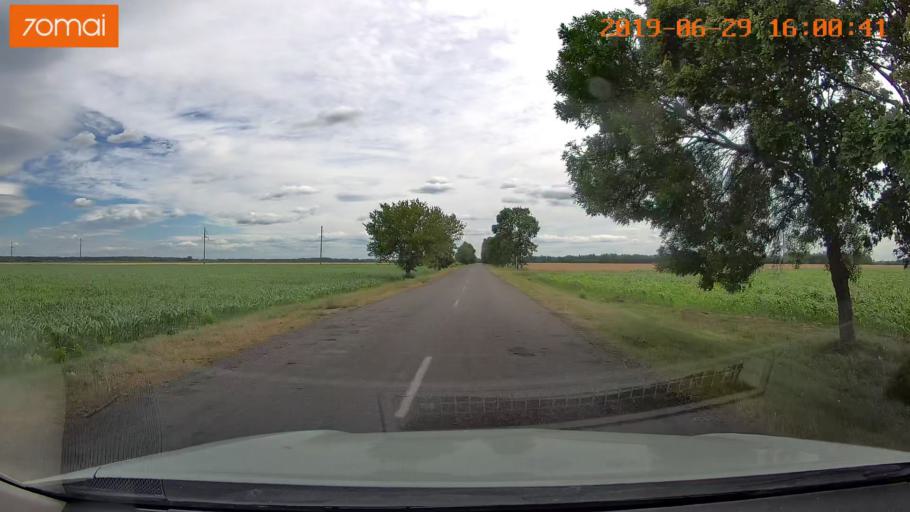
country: BY
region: Brest
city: Luninyets
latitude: 52.2572
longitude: 27.0172
